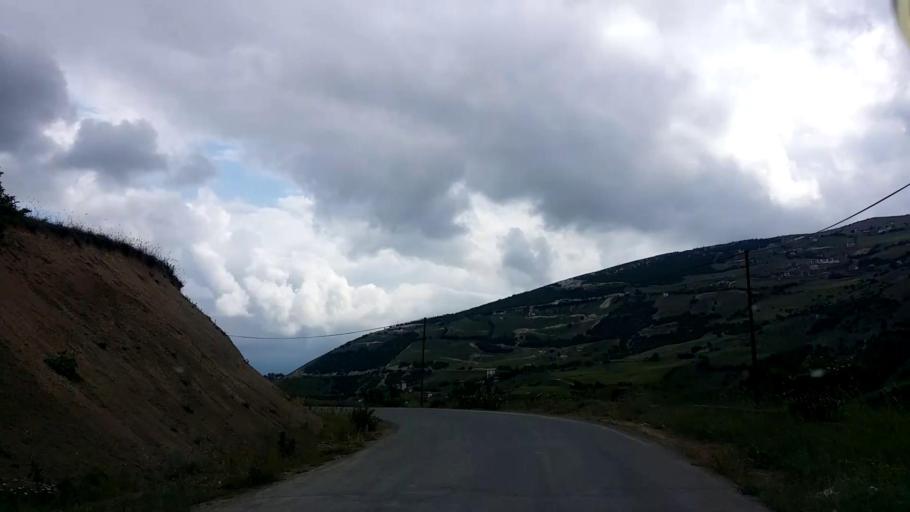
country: IR
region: Mazandaran
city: Chalus
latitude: 36.5525
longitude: 51.2801
